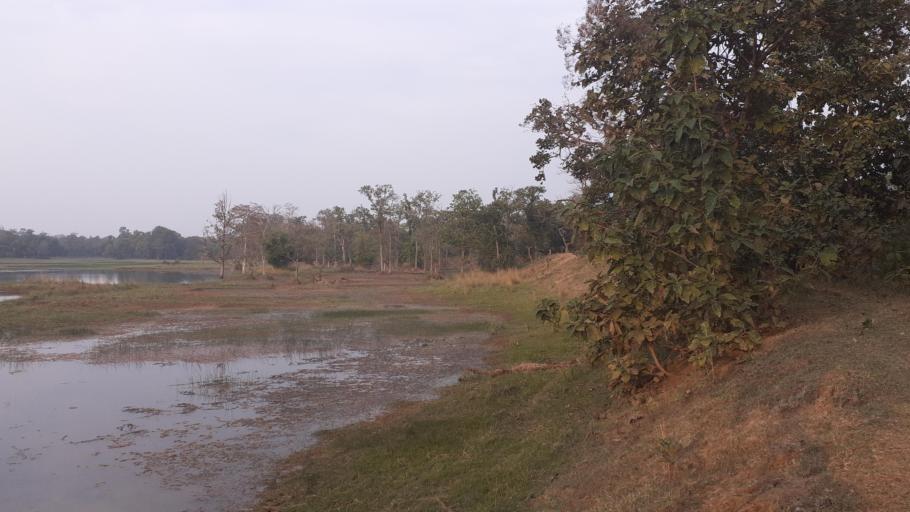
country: IN
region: Maharashtra
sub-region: Chandrapur
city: Mul
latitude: 20.0457
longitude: 79.4998
